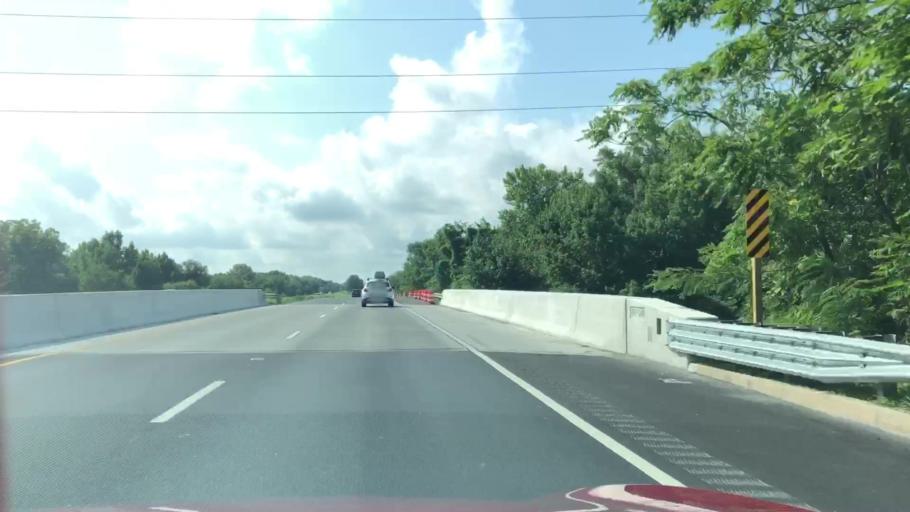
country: US
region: Maryland
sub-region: Wicomico County
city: Salisbury
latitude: 38.3805
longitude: -75.5404
